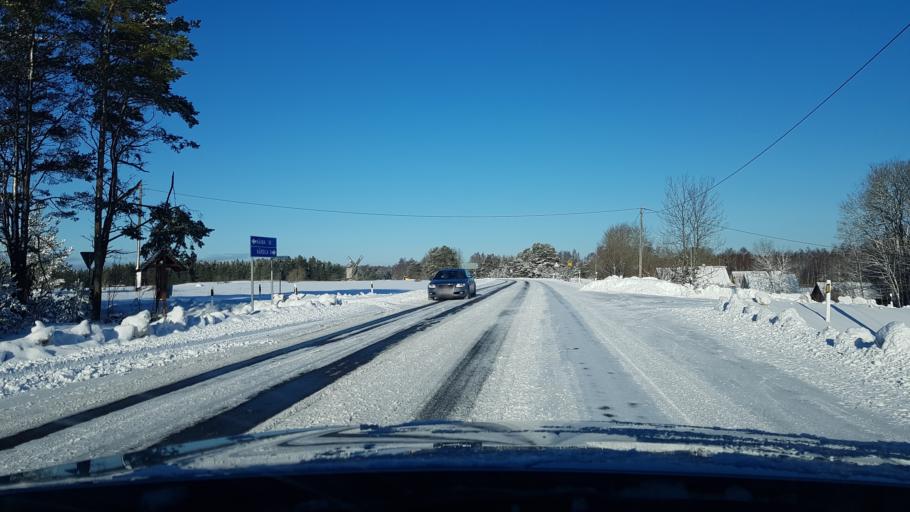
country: EE
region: Hiiumaa
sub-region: Kaerdla linn
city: Kardla
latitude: 58.9554
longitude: 22.7731
